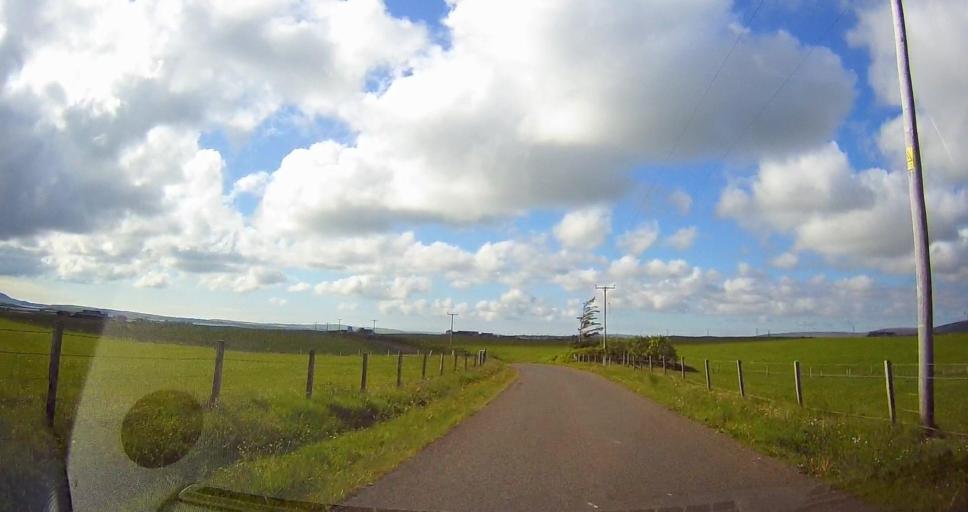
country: GB
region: Scotland
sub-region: Orkney Islands
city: Stromness
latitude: 58.9941
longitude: -3.1586
